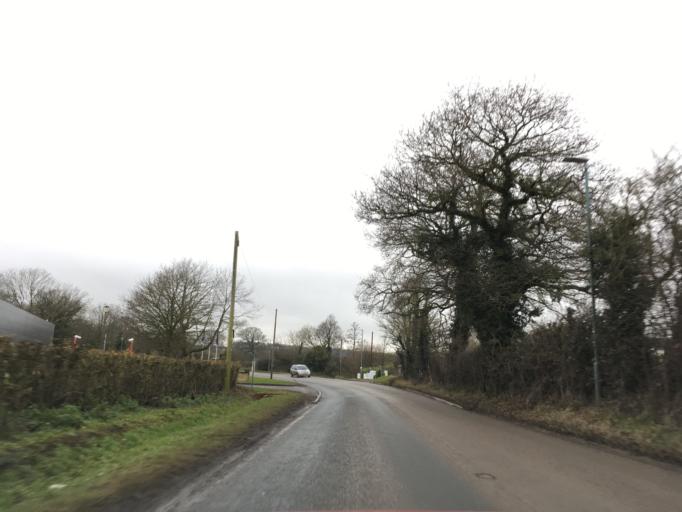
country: GB
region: England
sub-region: South Gloucestershire
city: Charfield
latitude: 51.6313
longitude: -2.3917
